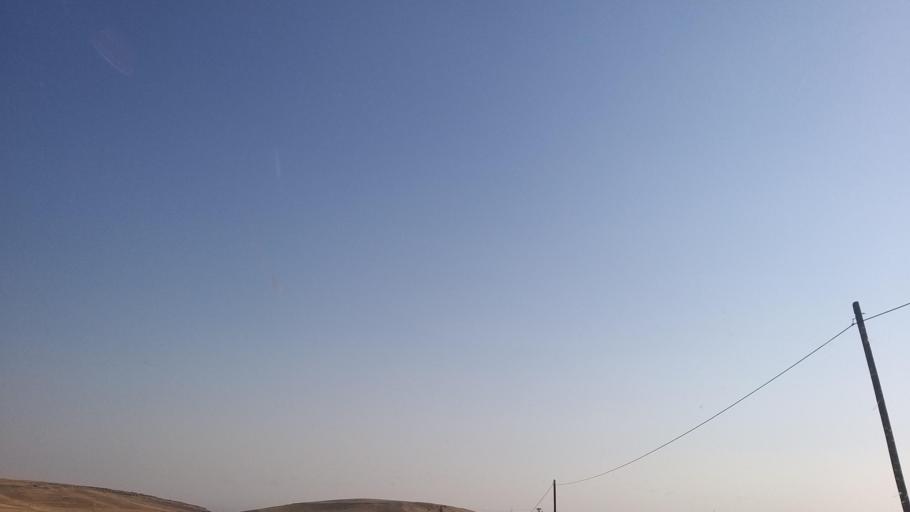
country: TR
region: Diyarbakir
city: Silvan
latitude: 38.1865
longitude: 41.0069
